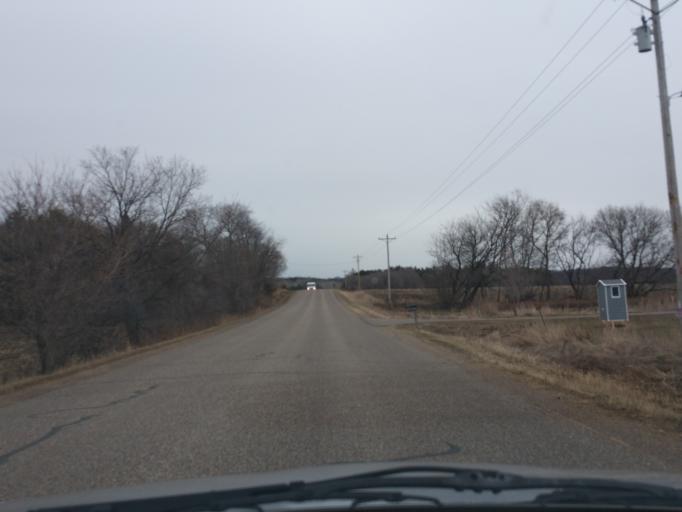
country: US
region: Wisconsin
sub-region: Saint Croix County
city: Roberts
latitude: 45.0035
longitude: -92.6359
